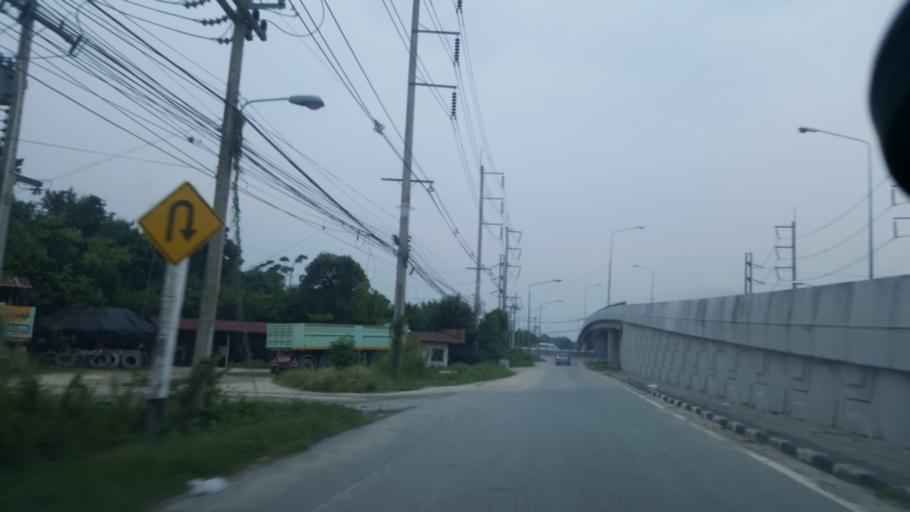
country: TH
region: Chon Buri
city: Si Racha
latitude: 13.2377
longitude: 100.9994
